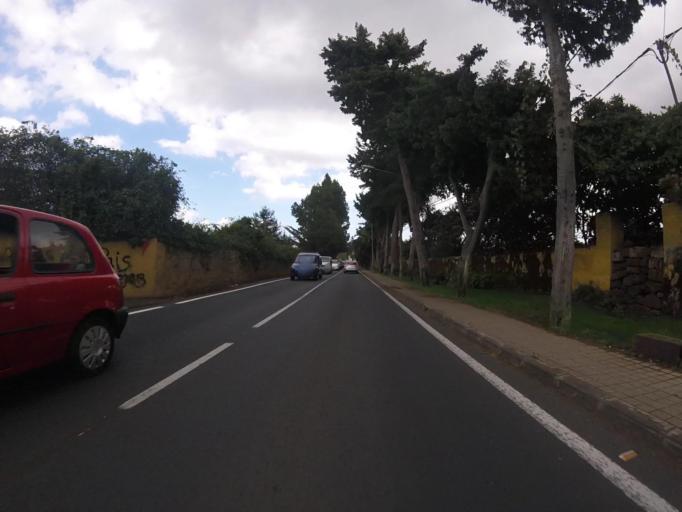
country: ES
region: Canary Islands
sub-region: Provincia de Las Palmas
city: Vega de San Mateo
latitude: 28.0206
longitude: -15.5220
